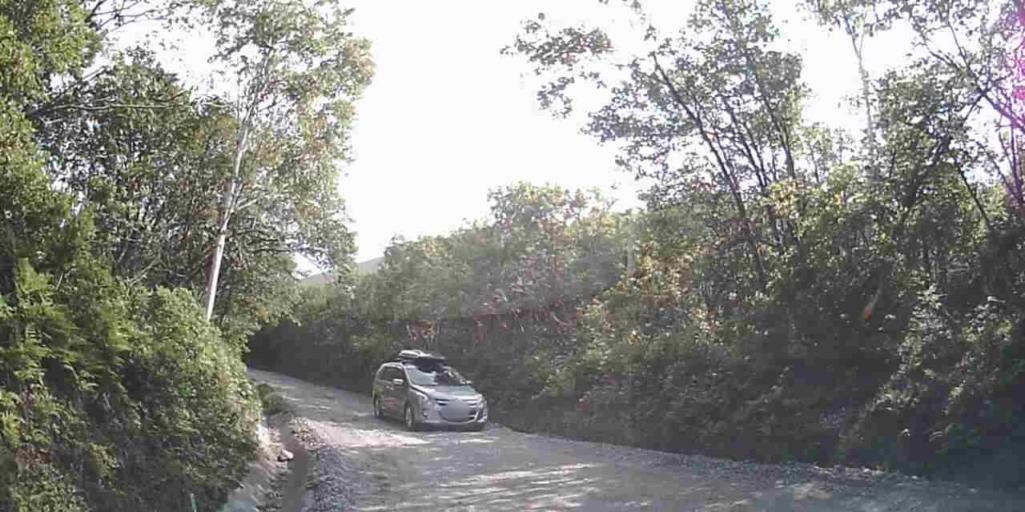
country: JP
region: Hokkaido
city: Shiraoi
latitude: 42.7018
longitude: 141.3911
